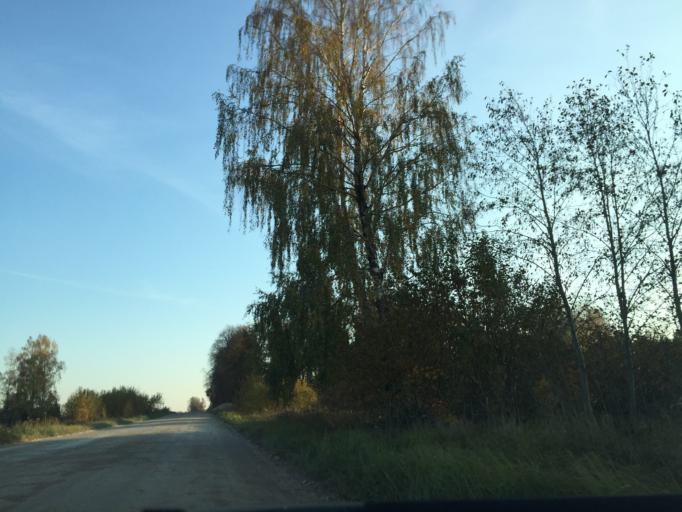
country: LV
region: Vainode
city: Vainode
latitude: 56.5216
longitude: 21.8275
